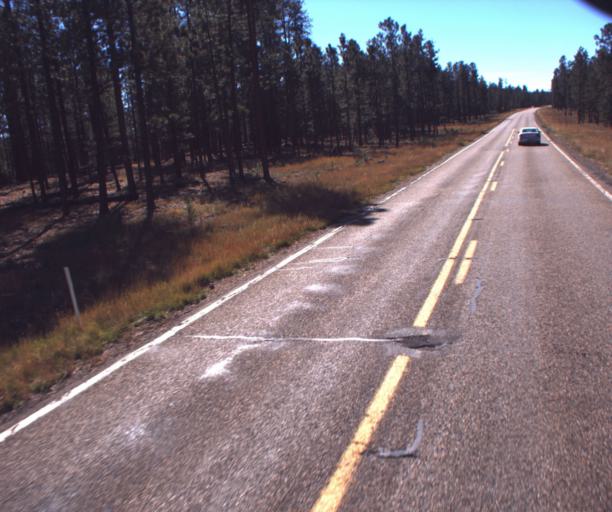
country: US
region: Arizona
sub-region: Coconino County
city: Fredonia
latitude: 36.7297
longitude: -112.2123
